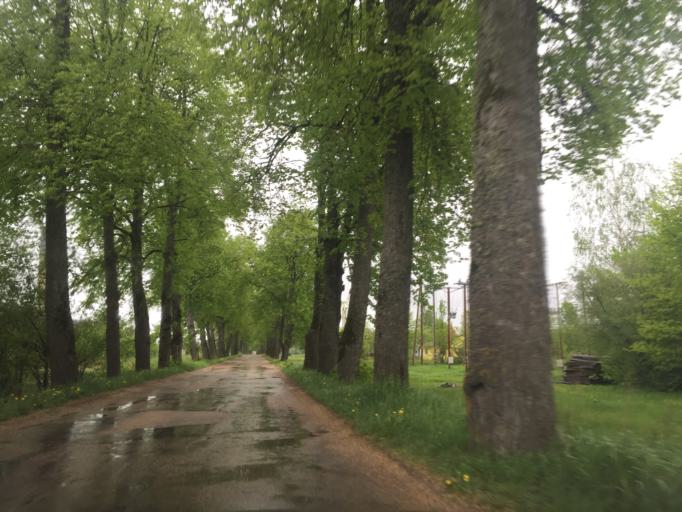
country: LV
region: Ogre
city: Jumprava
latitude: 56.6425
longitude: 24.9177
